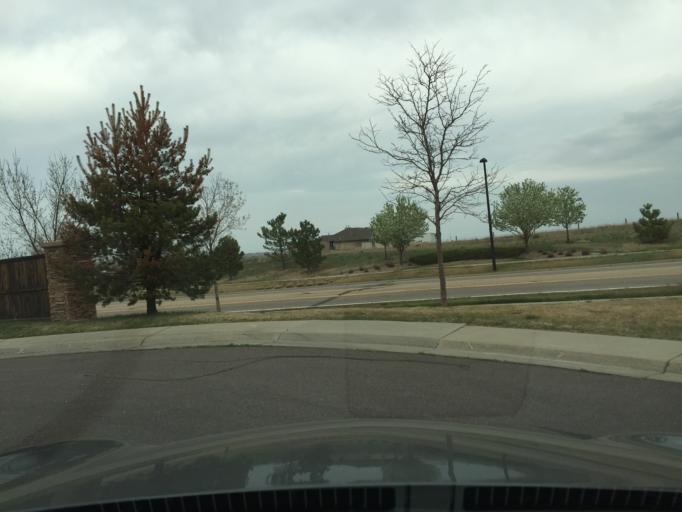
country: US
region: Colorado
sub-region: Boulder County
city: Erie
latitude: 40.0043
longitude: -105.0328
